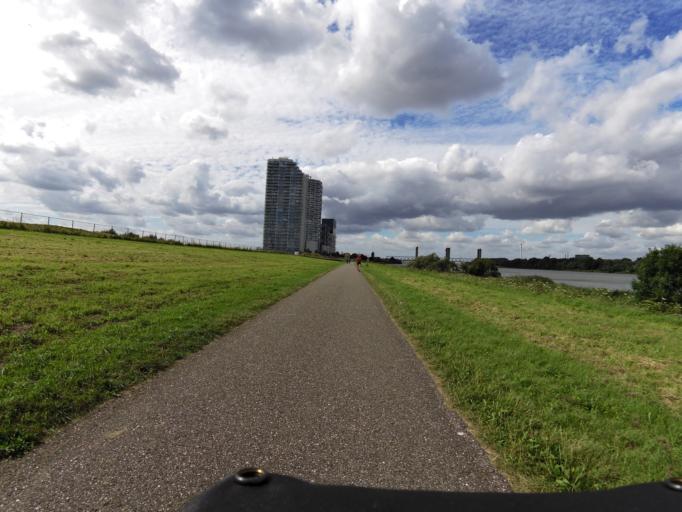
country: NL
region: South Holland
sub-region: Gemeente Spijkenisse
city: Spijkenisse
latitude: 51.8498
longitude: 4.3473
